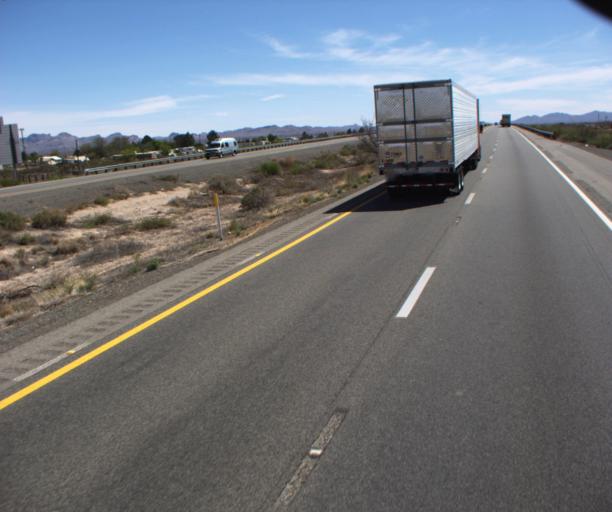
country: US
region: New Mexico
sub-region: Hidalgo County
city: Lordsburg
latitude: 32.2641
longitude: -109.2322
